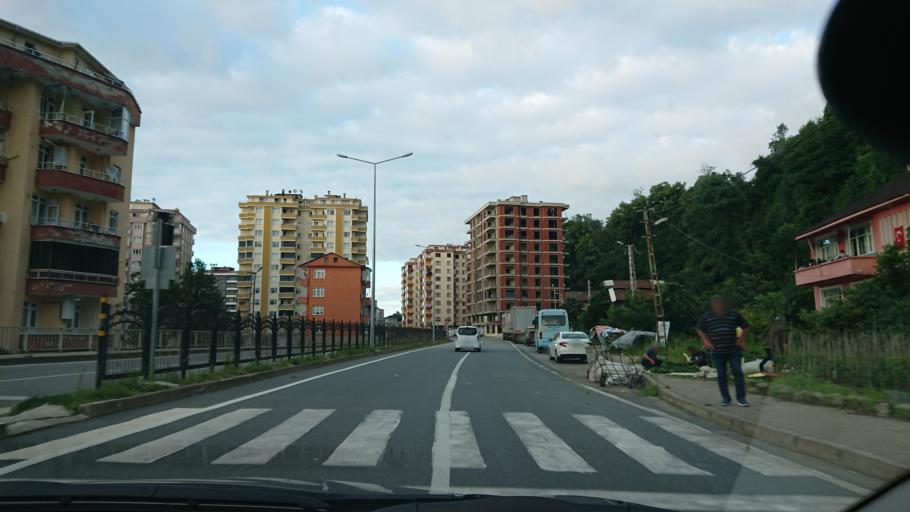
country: TR
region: Rize
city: Rize
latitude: 41.0317
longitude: 40.5600
